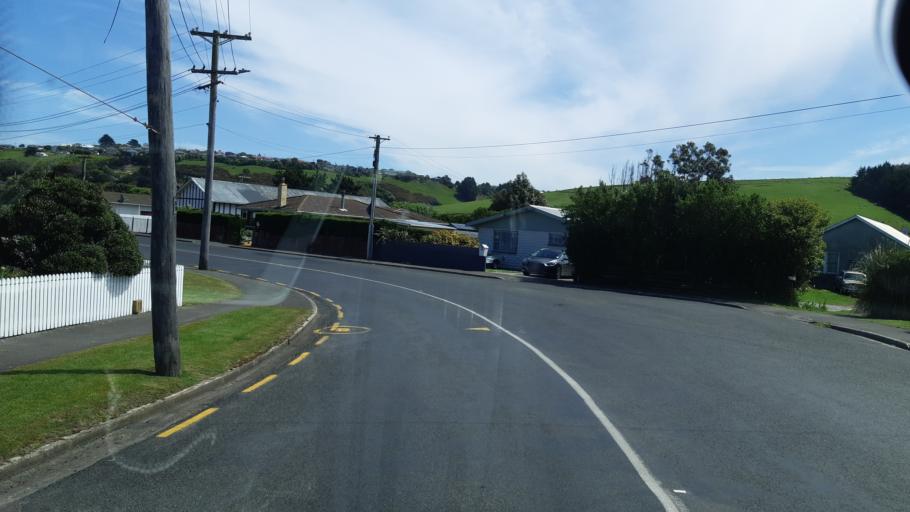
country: NZ
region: Otago
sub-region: Dunedin City
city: Dunedin
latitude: -45.9035
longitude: 170.5493
